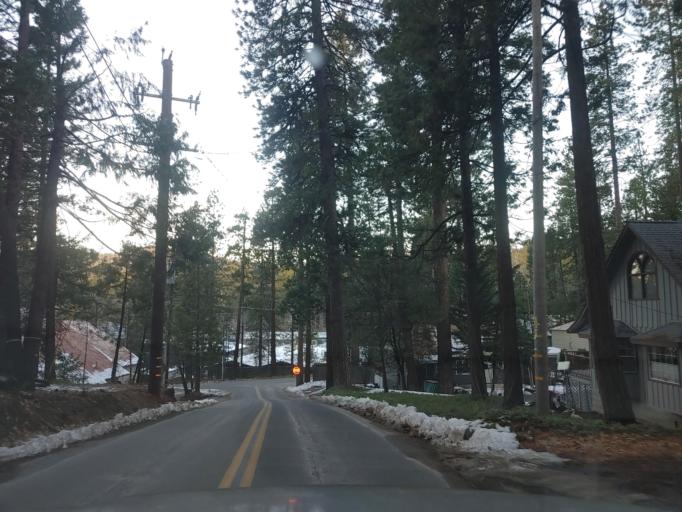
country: US
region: California
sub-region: Tuolumne County
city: Twain Harte
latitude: 38.0378
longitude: -120.2265
